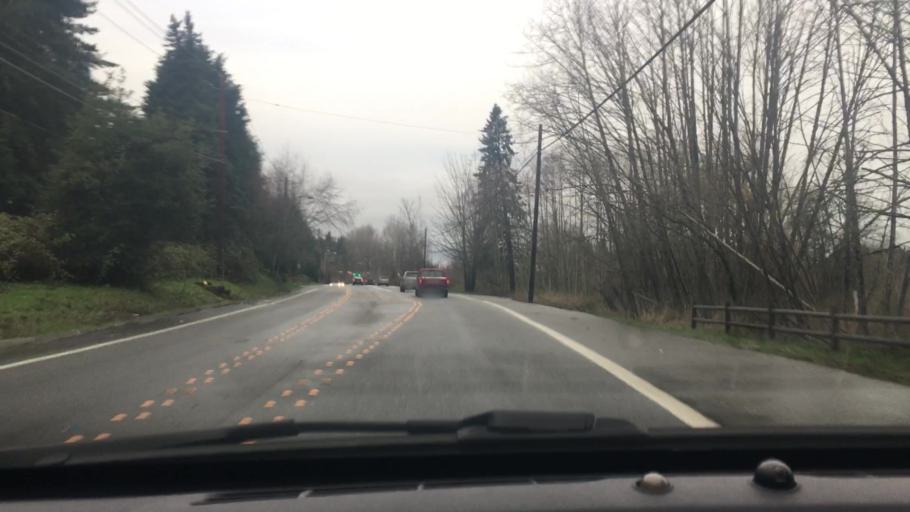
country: US
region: Washington
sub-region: King County
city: Redmond
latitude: 47.6550
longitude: -122.1182
